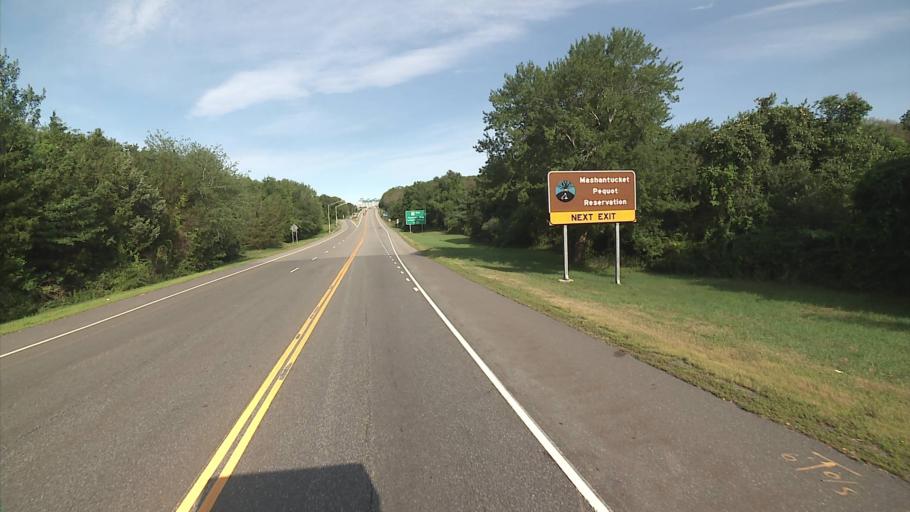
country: US
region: Connecticut
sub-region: New London County
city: Preston City
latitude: 41.4680
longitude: -71.9423
